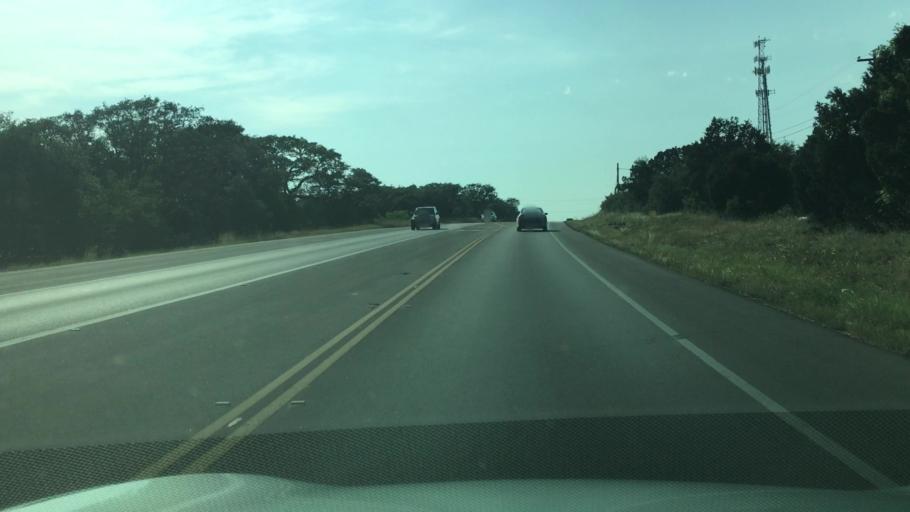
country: US
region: Texas
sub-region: Hays County
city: Wimberley
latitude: 29.9211
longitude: -98.0591
